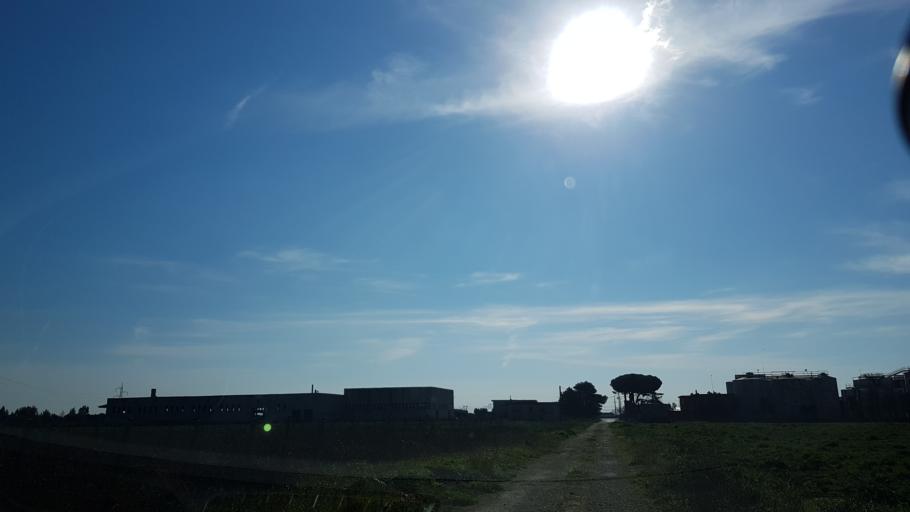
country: IT
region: Apulia
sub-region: Provincia di Brindisi
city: Brindisi
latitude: 40.6108
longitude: 17.8858
